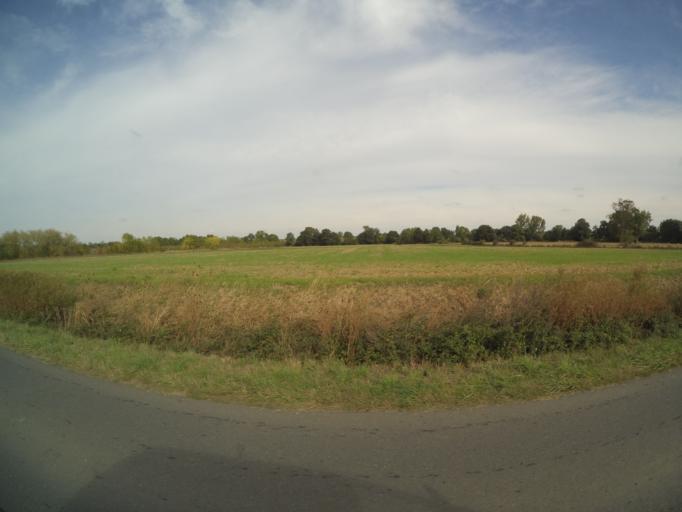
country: FR
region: Pays de la Loire
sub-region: Departement de Maine-et-Loire
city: Saint-Jean
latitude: 47.2024
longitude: -0.3798
